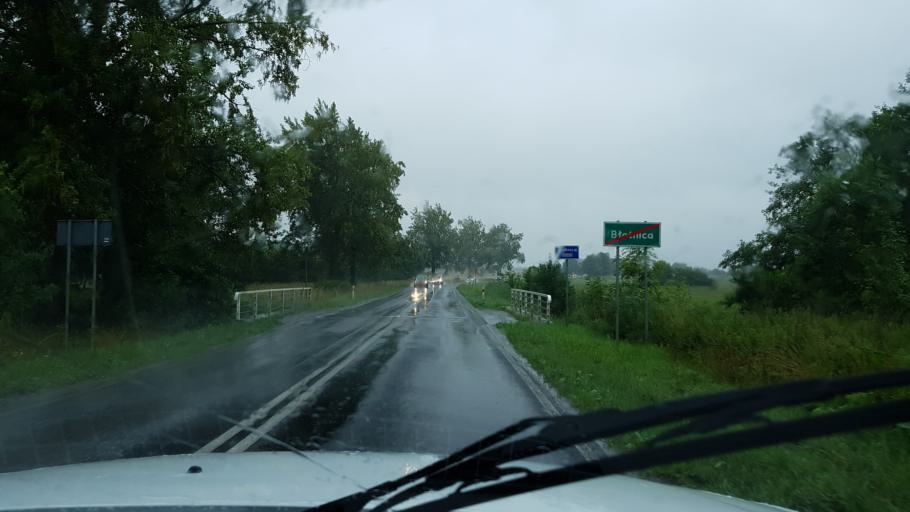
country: PL
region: West Pomeranian Voivodeship
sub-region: Powiat kolobrzeski
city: Grzybowo
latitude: 54.1027
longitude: 15.5142
